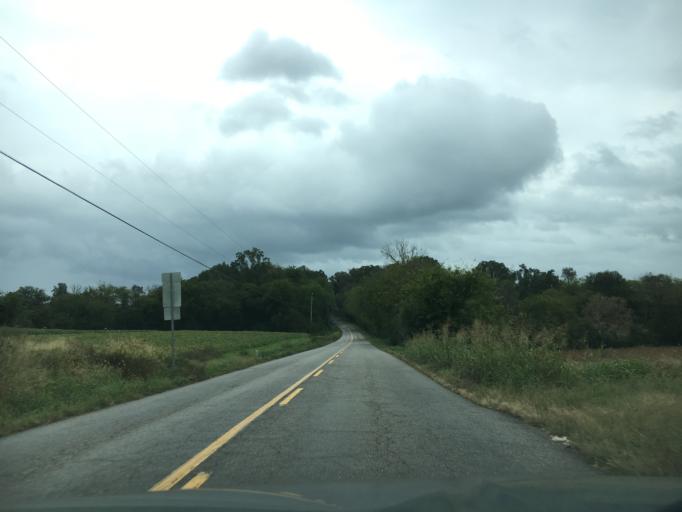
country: US
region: Virginia
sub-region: Amelia County
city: Amelia Court House
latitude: 37.3947
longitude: -77.9735
